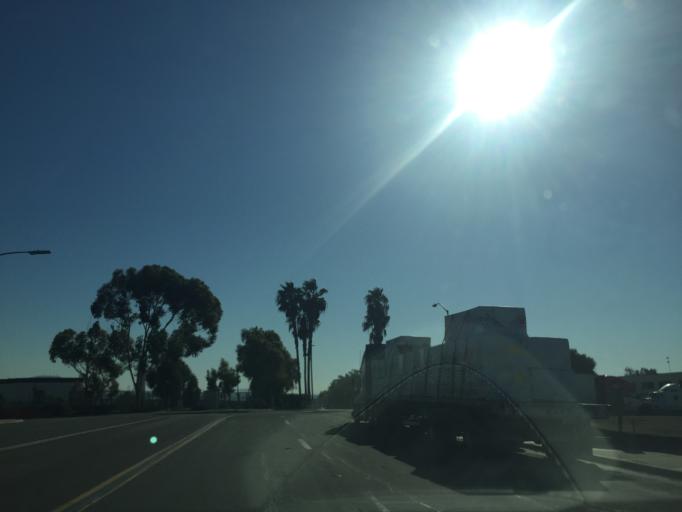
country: MX
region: Baja California
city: Tijuana
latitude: 32.5534
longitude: -116.9279
